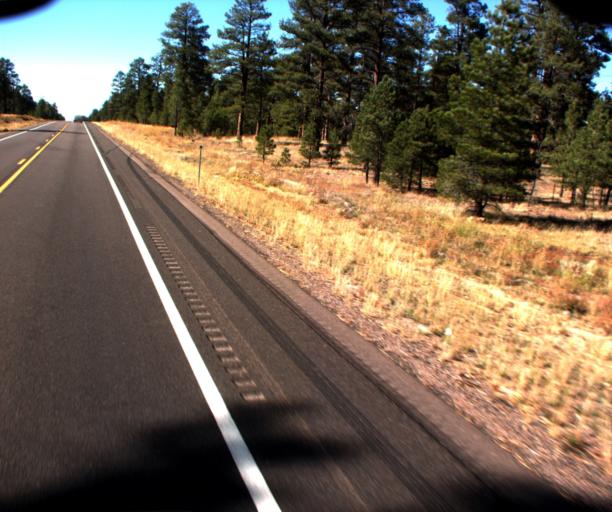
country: US
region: Arizona
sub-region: Apache County
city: Saint Michaels
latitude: 35.6932
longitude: -109.2646
